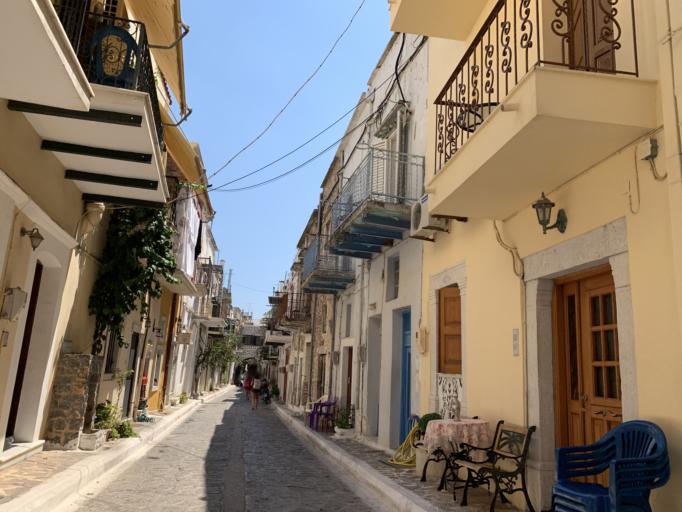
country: GR
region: North Aegean
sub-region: Chios
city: Thymiana
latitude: 38.2271
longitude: 25.9975
